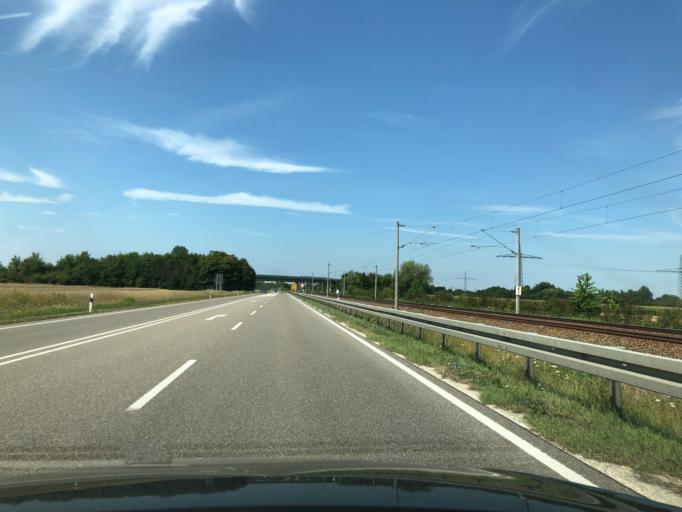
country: DE
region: Bavaria
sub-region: Upper Bavaria
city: Karlskron
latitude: 48.7082
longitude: 11.4276
